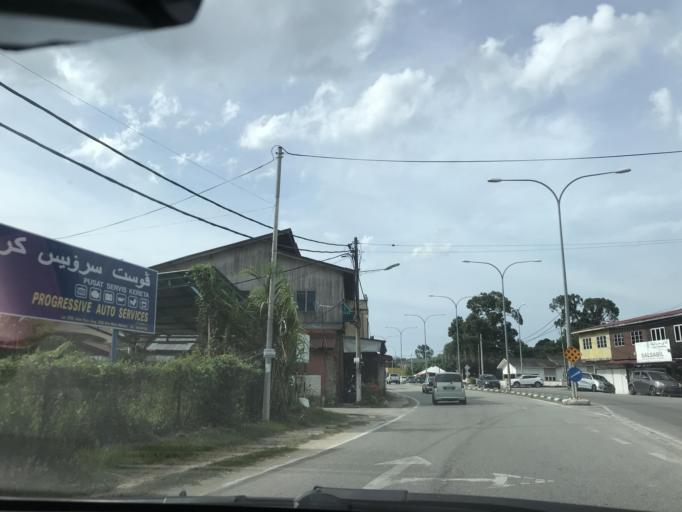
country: MY
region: Kelantan
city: Kota Bharu
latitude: 6.0900
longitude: 102.2290
